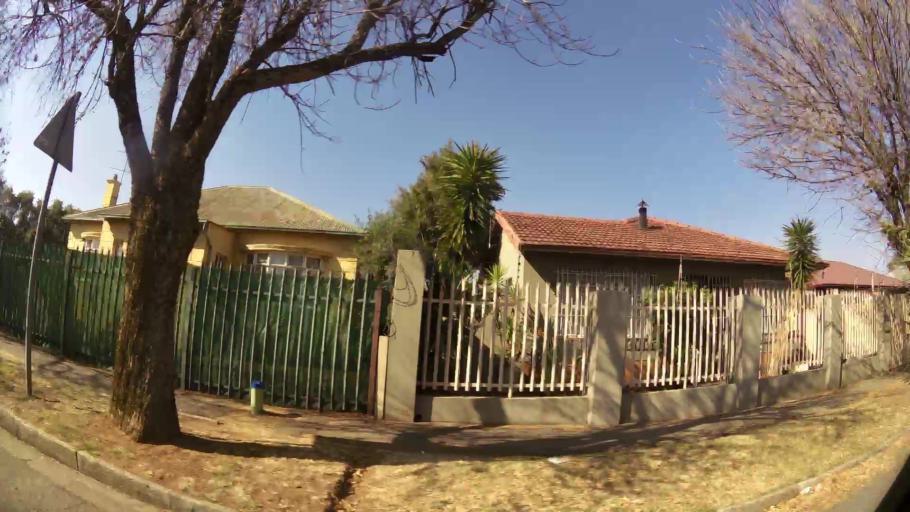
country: ZA
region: Gauteng
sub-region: City of Johannesburg Metropolitan Municipality
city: Johannesburg
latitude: -26.2598
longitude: 28.0512
